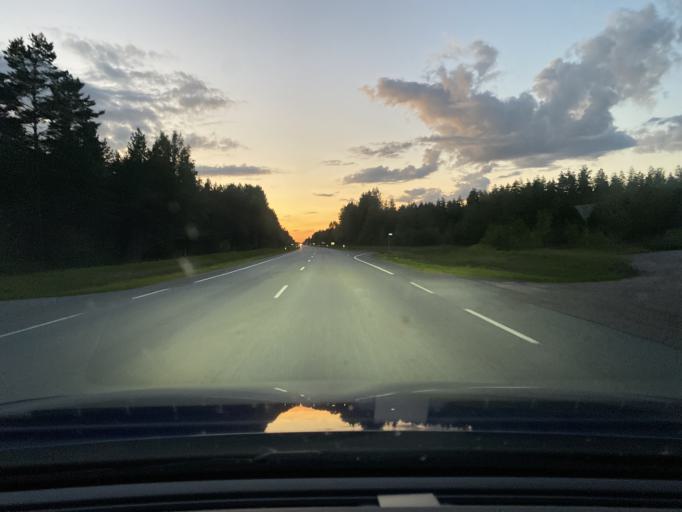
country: FI
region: Varsinais-Suomi
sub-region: Loimaa
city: Oripaeae
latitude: 60.8988
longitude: 22.7000
